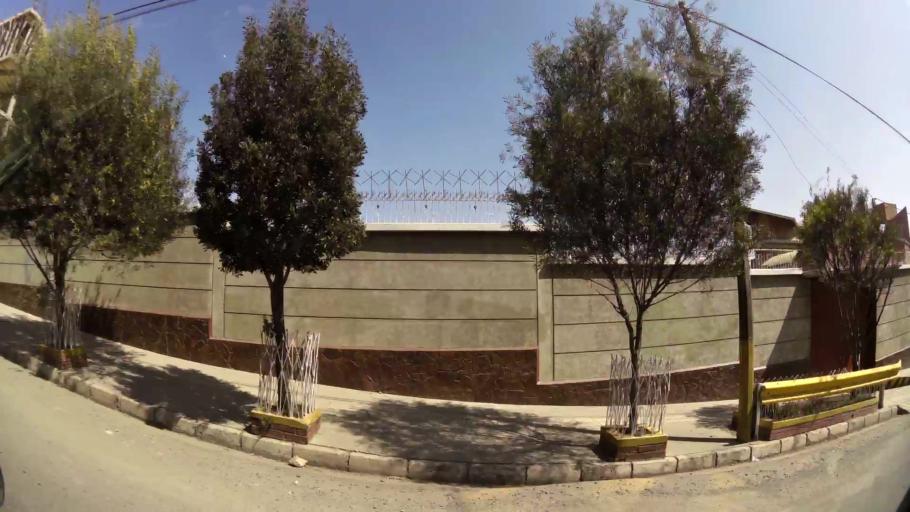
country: BO
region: La Paz
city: La Paz
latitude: -16.5400
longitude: -68.0557
